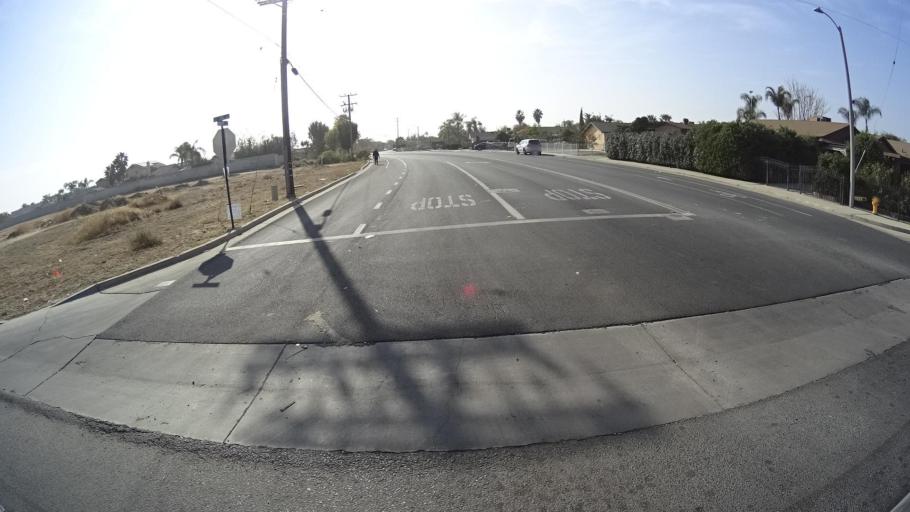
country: US
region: California
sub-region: Kern County
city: Delano
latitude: 35.7904
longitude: -119.2325
